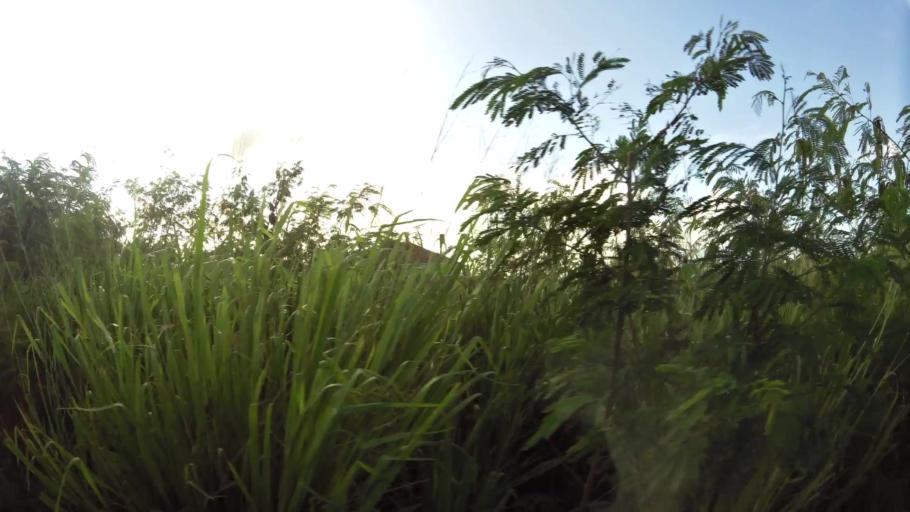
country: AG
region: Saint John
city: Potters Village
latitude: 17.0912
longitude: -61.8042
